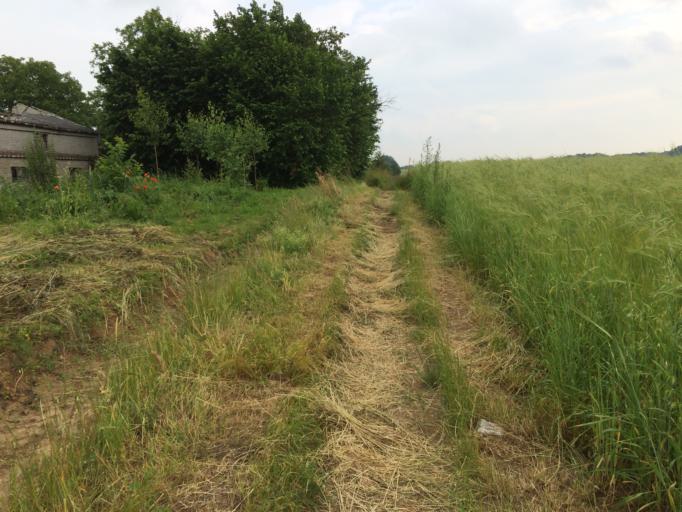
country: PL
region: Lublin Voivodeship
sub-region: Powiat pulawski
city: Markuszow
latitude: 51.3490
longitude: 22.2516
